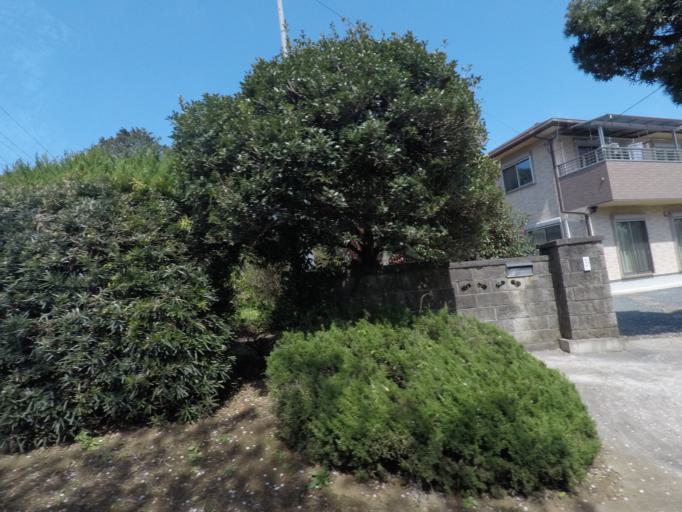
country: JP
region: Chiba
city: Narita
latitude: 35.7845
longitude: 140.3422
